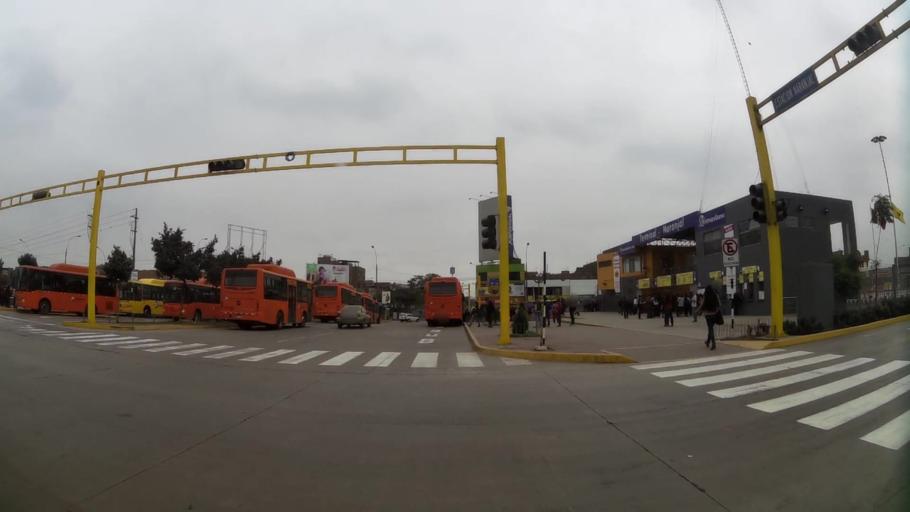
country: PE
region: Lima
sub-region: Lima
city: Independencia
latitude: -11.9829
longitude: -77.0582
